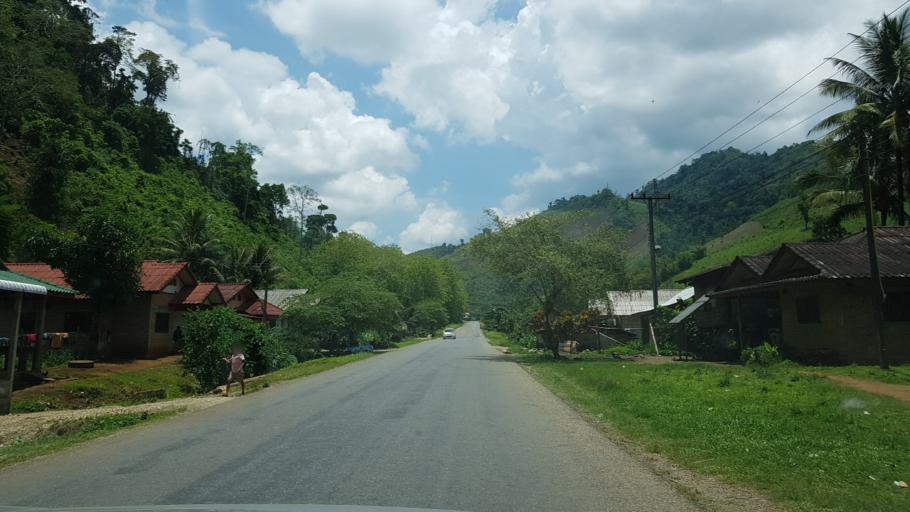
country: LA
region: Vientiane
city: Muang Kasi
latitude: 19.1322
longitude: 102.2802
